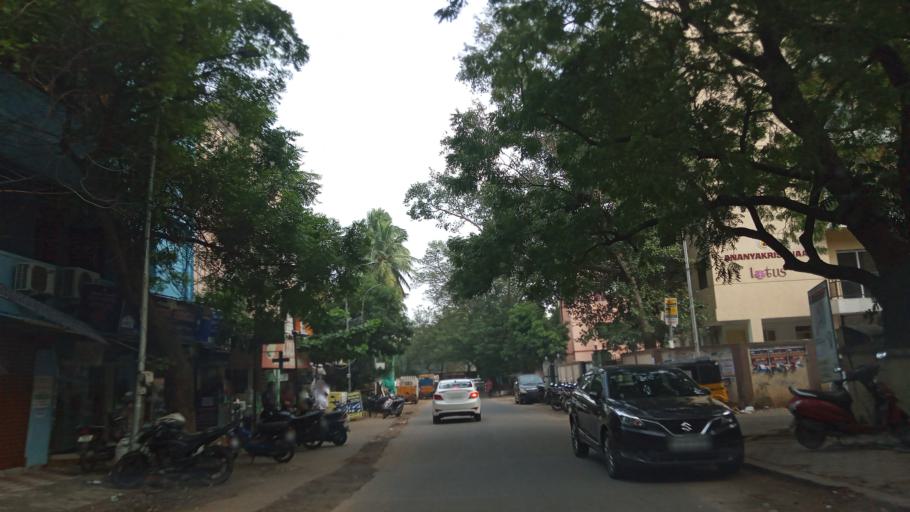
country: IN
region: Tamil Nadu
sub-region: Kancheepuram
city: Alandur
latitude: 13.0373
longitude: 80.2153
